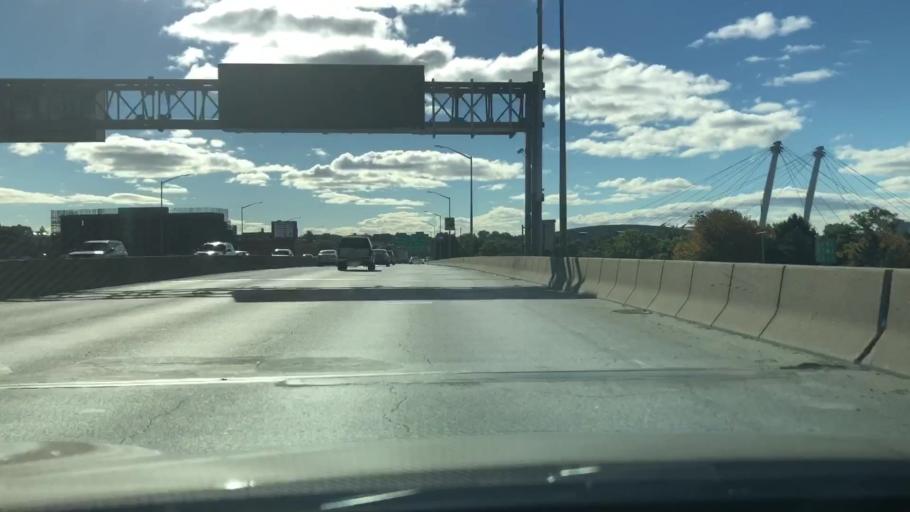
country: US
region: New York
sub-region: Queens County
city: Jamaica
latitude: 40.7538
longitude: -73.8377
